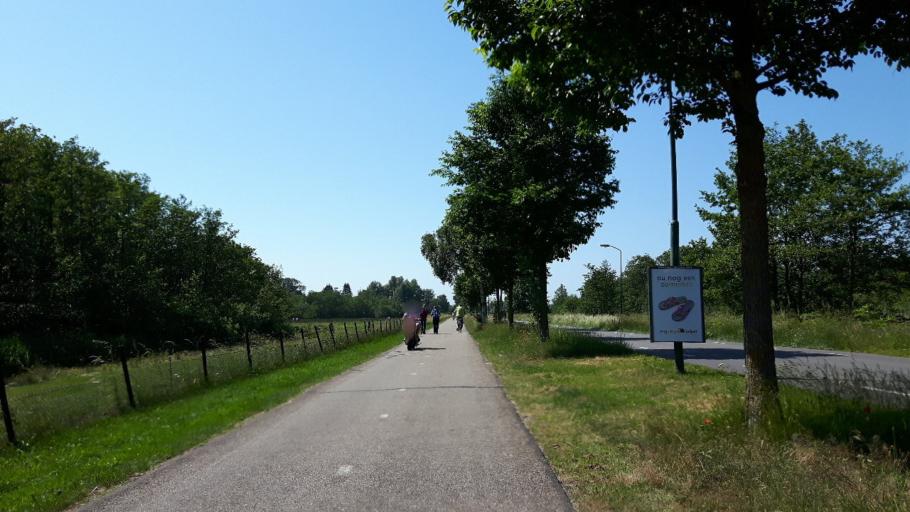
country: NL
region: North Holland
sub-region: Gemeente Wijdemeren
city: Kortenhoef
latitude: 52.2536
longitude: 5.1009
